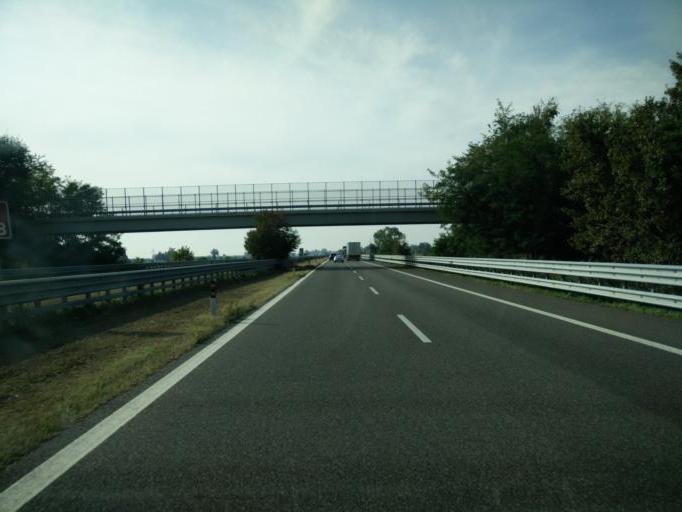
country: IT
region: Lombardy
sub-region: Provincia di Cremona
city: San Felice
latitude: 45.1649
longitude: 10.0807
